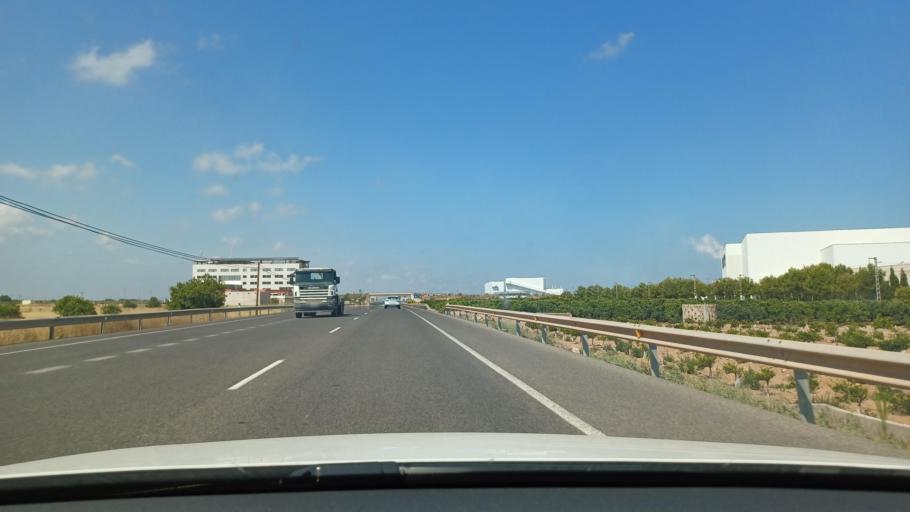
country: ES
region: Valencia
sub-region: Provincia de Castello
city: Chilches
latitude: 39.7931
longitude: -0.1825
